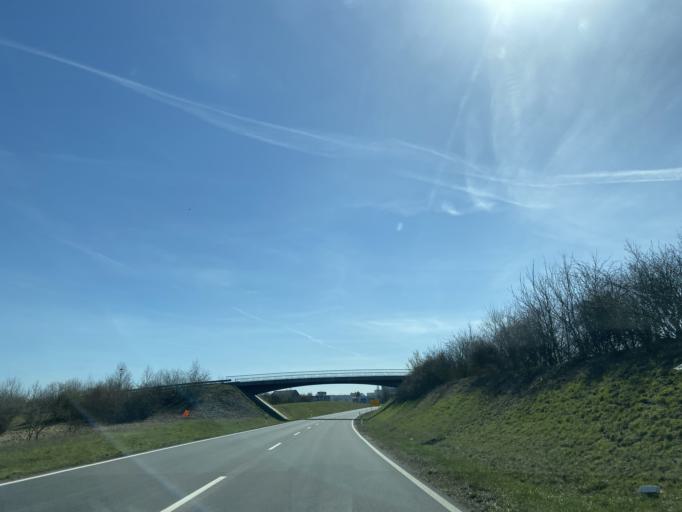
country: DE
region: Baden-Wuerttemberg
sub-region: Regierungsbezirk Stuttgart
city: Rutesheim
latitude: 48.8148
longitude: 8.9531
